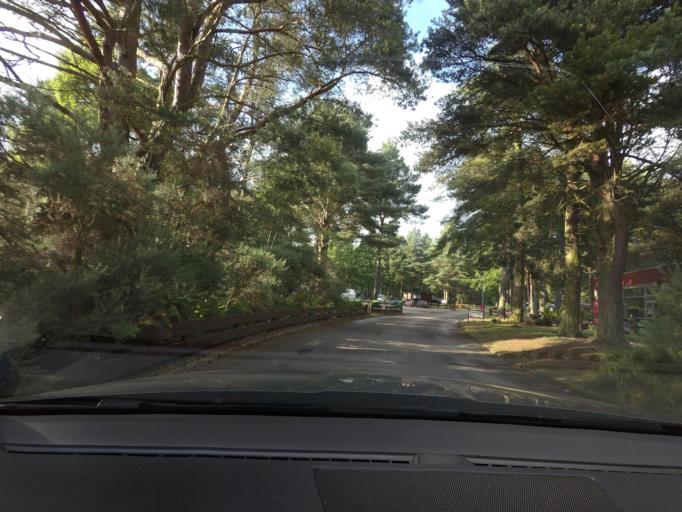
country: GB
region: Scotland
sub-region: Highland
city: Nairn
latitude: 57.5714
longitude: -3.9297
